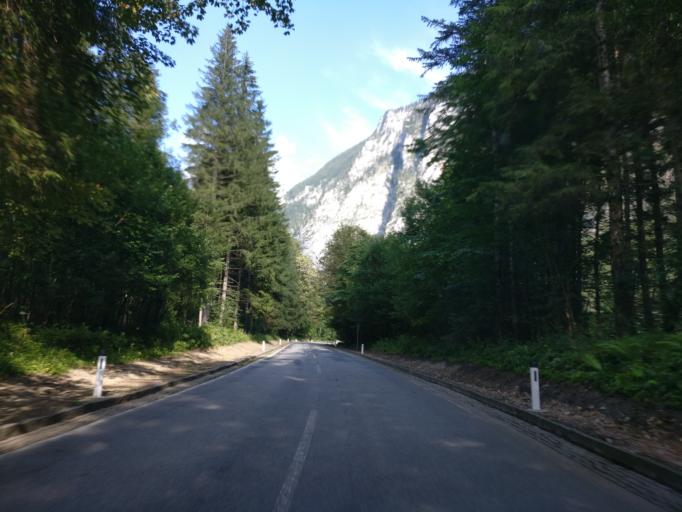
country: AT
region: Styria
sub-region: Politischer Bezirk Leoben
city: Hieflau
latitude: 47.5883
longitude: 14.6654
